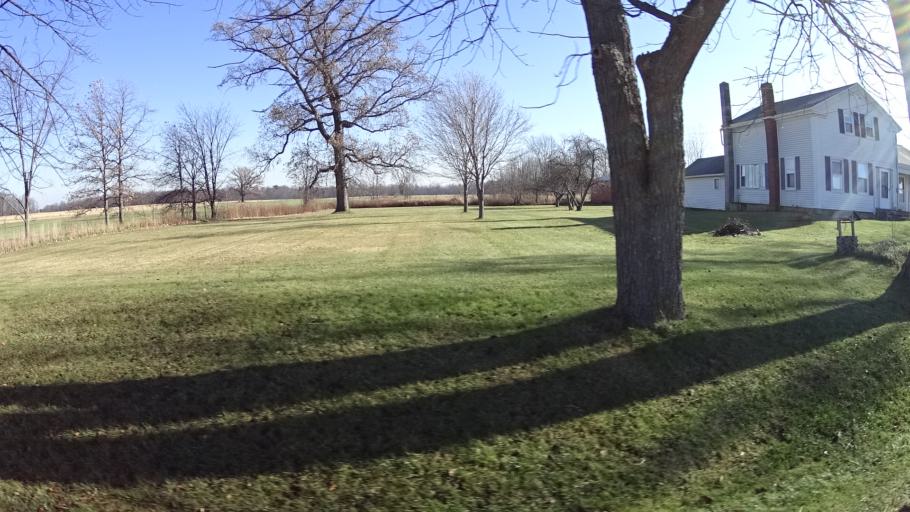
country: US
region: Ohio
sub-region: Huron County
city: New London
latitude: 41.0943
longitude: -82.3283
